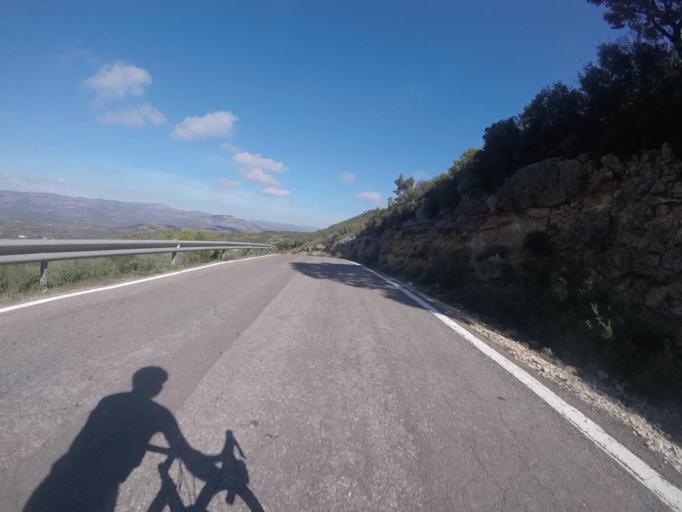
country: ES
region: Valencia
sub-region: Provincia de Castello
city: Albocasser
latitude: 40.3477
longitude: 0.0495
